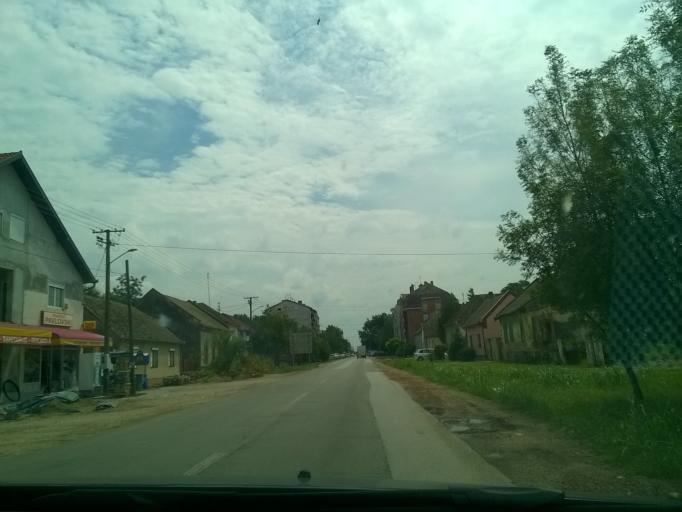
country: RS
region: Autonomna Pokrajina Vojvodina
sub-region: Juznobanatski Okrug
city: Plandiste
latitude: 45.2309
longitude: 21.1192
